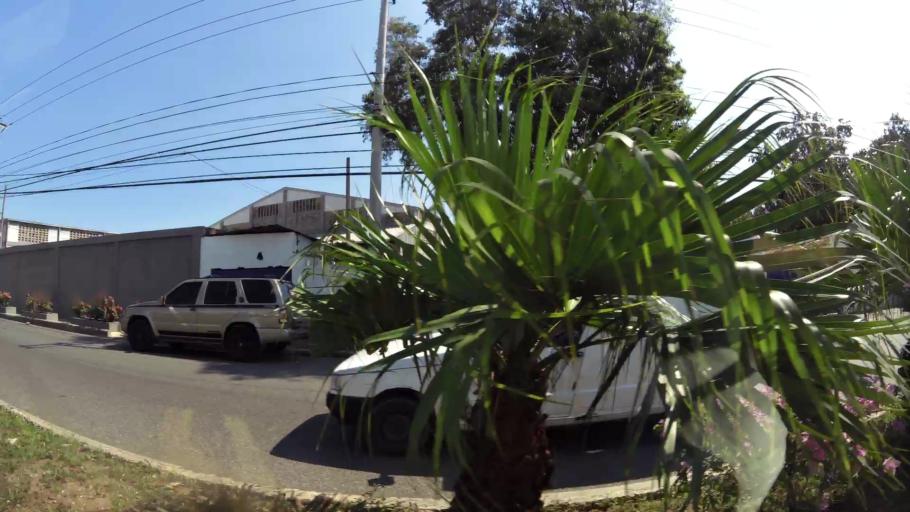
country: DO
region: Nacional
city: Santo Domingo
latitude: 18.4851
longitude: -69.9869
